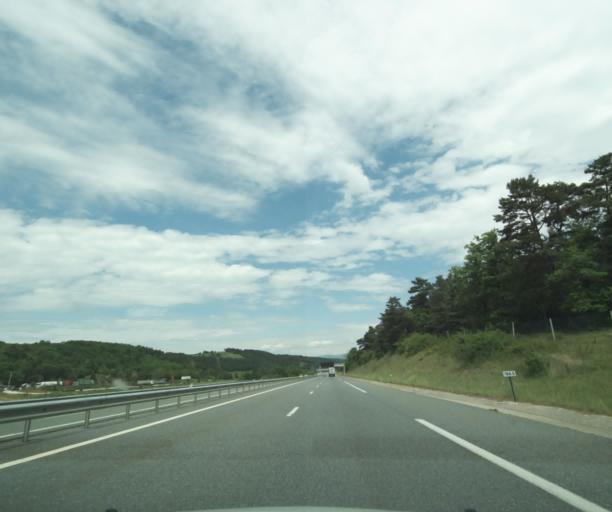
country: FR
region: Midi-Pyrenees
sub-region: Departement de l'Aveyron
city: Severac-le-Chateau
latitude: 44.3654
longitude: 3.1168
